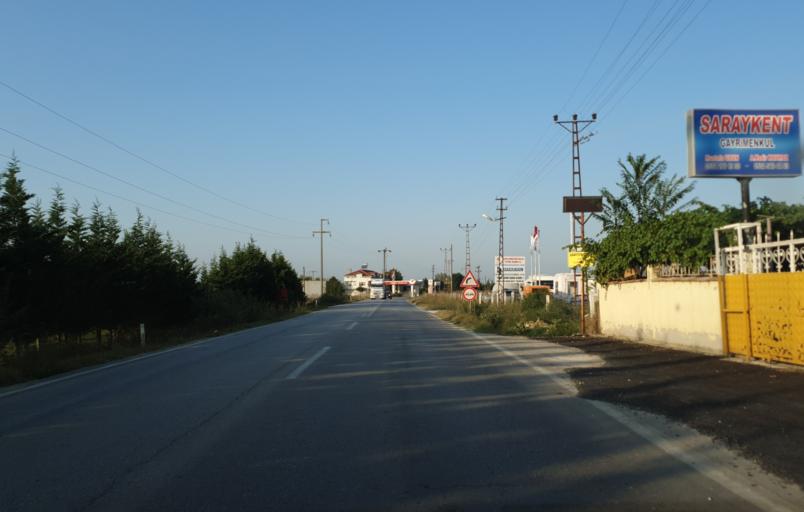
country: TR
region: Tekirdag
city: Saray
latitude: 41.4335
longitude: 27.8969
